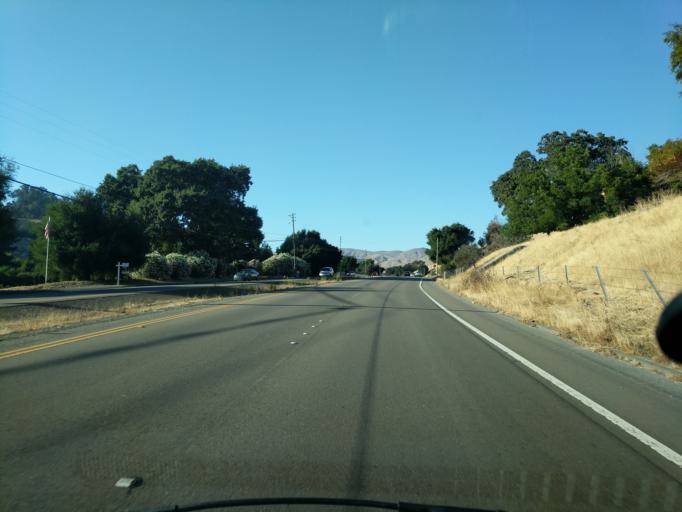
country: US
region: California
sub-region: Contra Costa County
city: San Ramon
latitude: 37.7426
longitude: -122.0315
